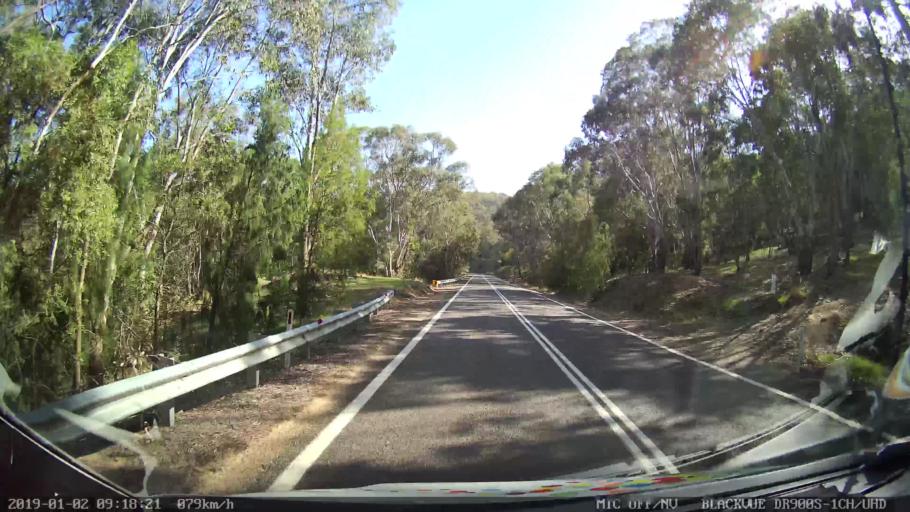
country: AU
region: New South Wales
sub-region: Tumut Shire
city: Tumut
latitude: -35.4300
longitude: 148.2859
